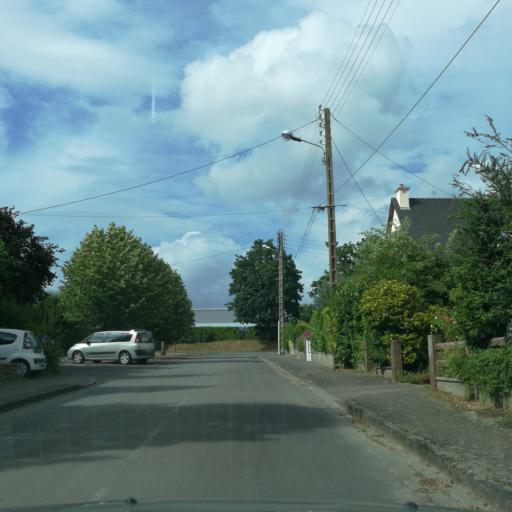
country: FR
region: Brittany
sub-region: Departement d'Ille-et-Vilaine
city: Montauban-de-Bretagne
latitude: 48.1957
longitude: -2.0476
